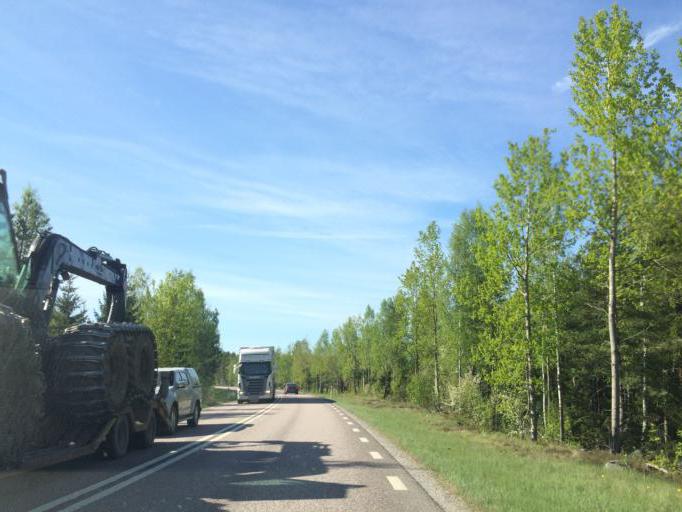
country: SE
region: Soedermanland
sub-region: Katrineholms Kommun
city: Katrineholm
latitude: 59.1362
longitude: 16.1361
